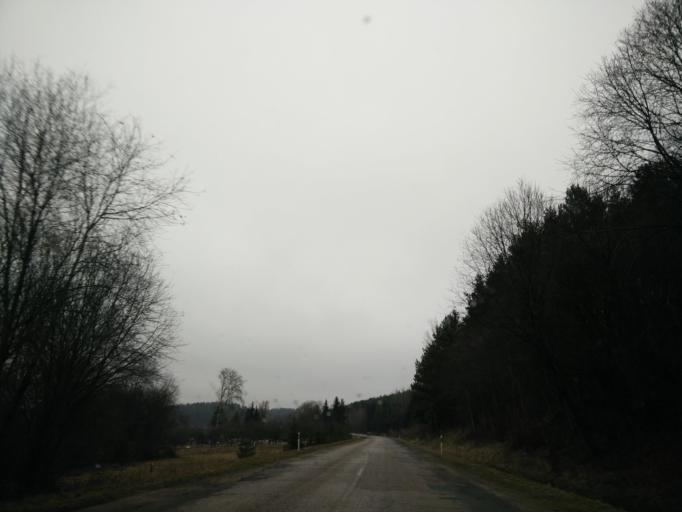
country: LT
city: Ariogala
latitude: 55.2906
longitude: 23.4431
